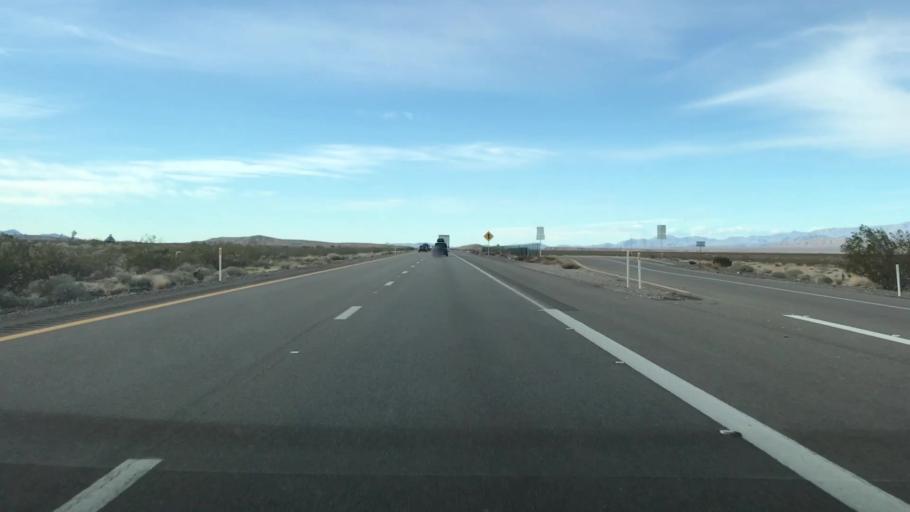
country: US
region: Nevada
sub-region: Clark County
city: Moapa Town
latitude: 36.6316
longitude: -114.6070
